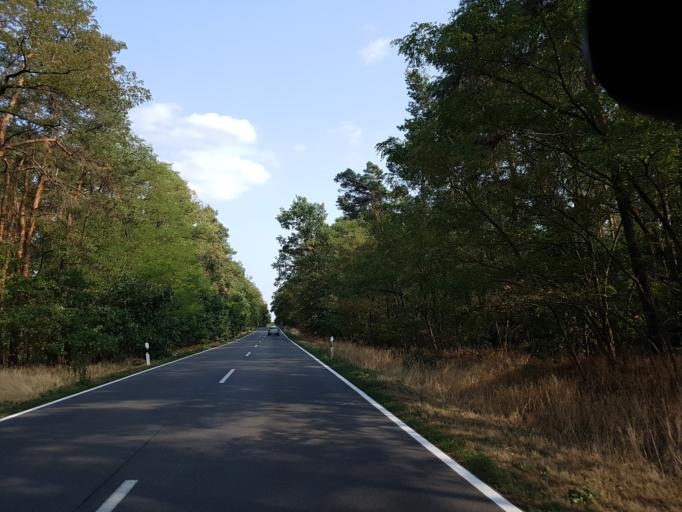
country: DE
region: Saxony-Anhalt
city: Pretzsch
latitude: 51.7341
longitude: 12.7676
